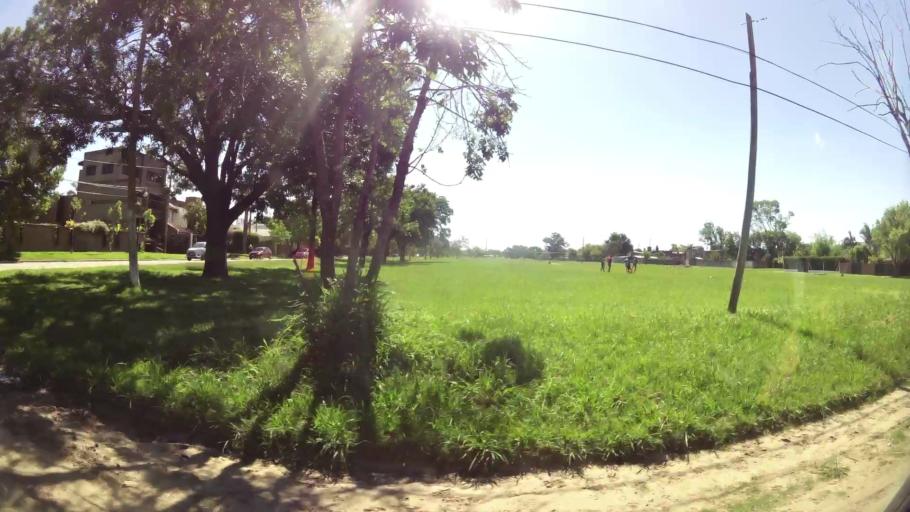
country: AR
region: Santa Fe
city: Santa Fe de la Vera Cruz
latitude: -31.5991
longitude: -60.6699
